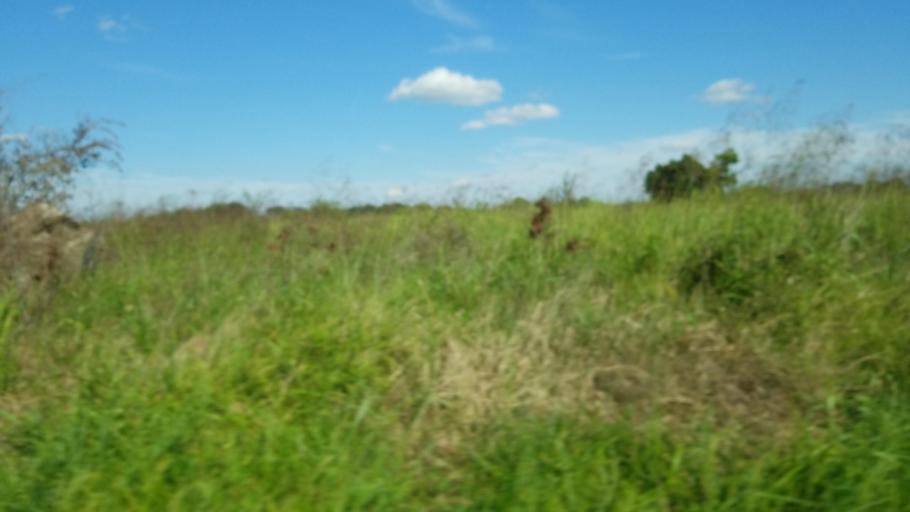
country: US
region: Illinois
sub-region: Saline County
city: Harrisburg
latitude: 37.8309
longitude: -88.5720
